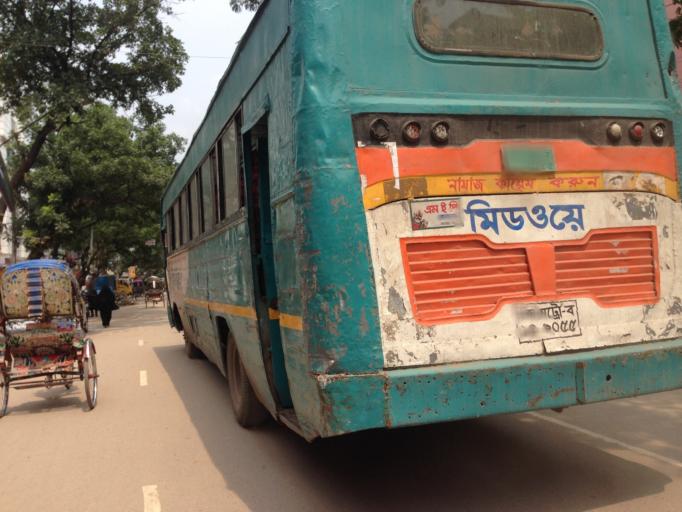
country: BD
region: Dhaka
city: Paltan
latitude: 23.7525
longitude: 90.4207
